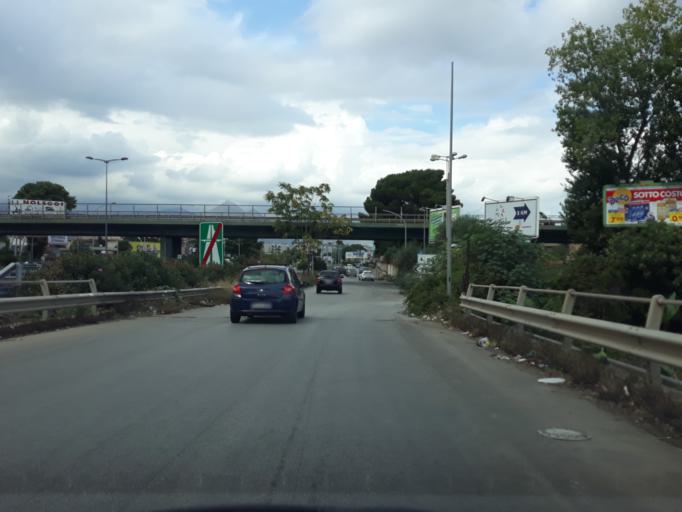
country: IT
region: Sicily
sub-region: Palermo
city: Ciaculli
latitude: 38.0898
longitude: 13.3855
